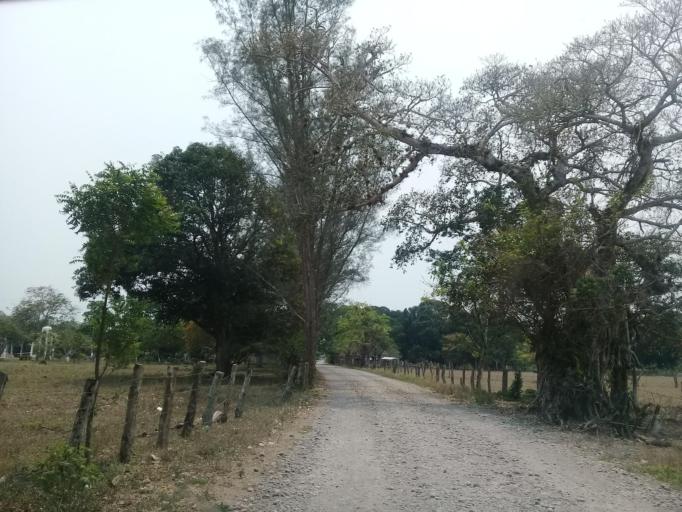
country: MX
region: Veracruz
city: Jamapa
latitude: 18.9332
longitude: -96.2144
